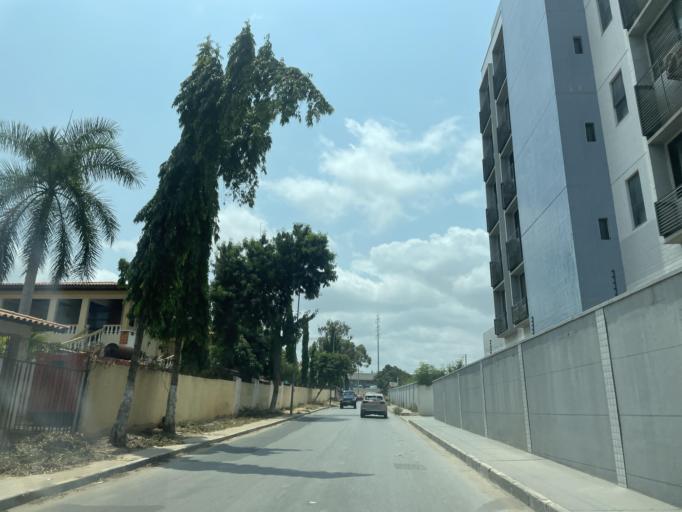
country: AO
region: Luanda
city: Luanda
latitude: -8.9096
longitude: 13.1958
